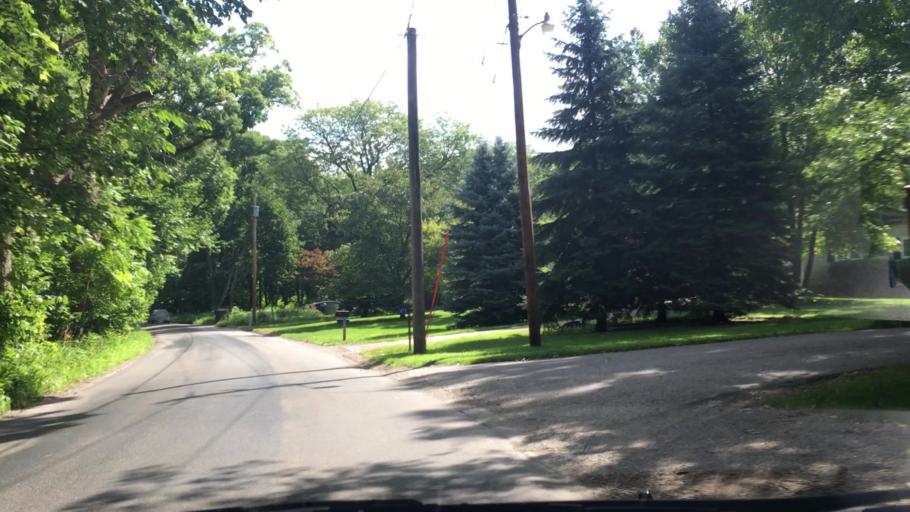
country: US
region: Iowa
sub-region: Johnson County
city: Iowa City
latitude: 41.6897
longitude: -91.5357
